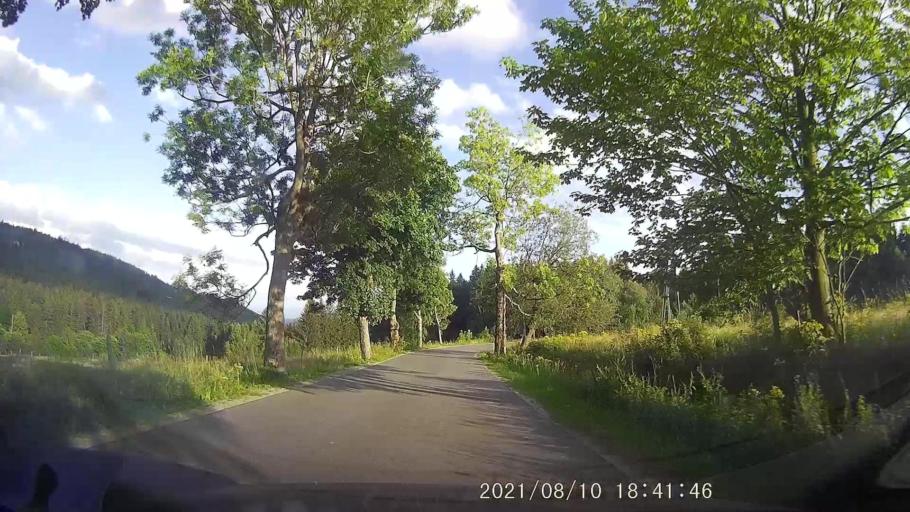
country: PL
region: Lower Silesian Voivodeship
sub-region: Powiat klodzki
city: Duszniki-Zdroj
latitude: 50.4540
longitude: 16.3428
